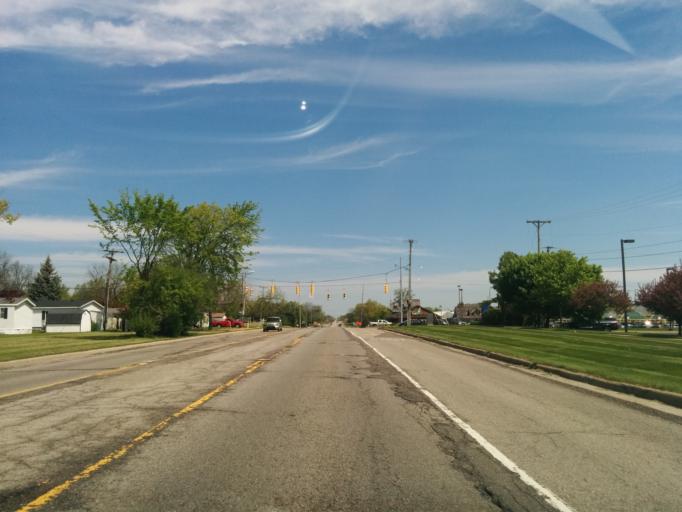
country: US
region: Michigan
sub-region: Oakland County
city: Novi
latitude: 42.4889
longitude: -83.4359
